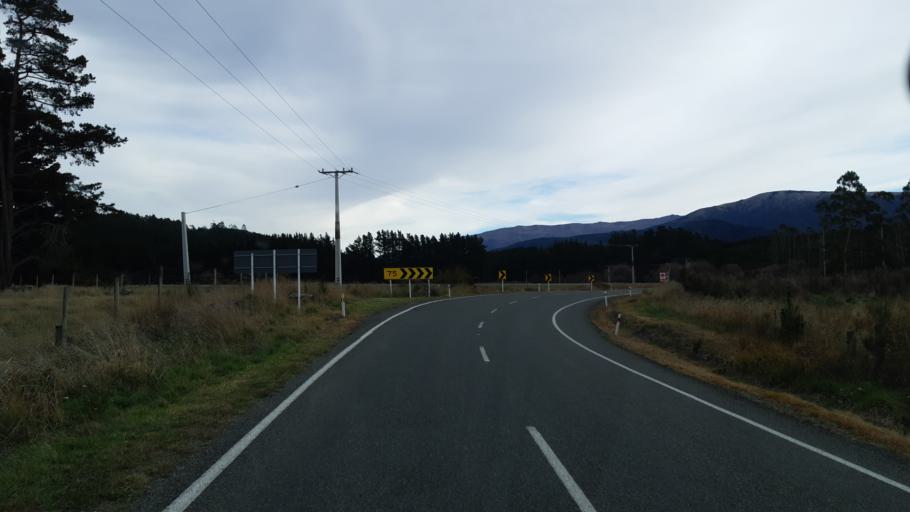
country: NZ
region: Tasman
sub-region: Tasman District
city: Brightwater
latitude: -41.6576
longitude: 173.2373
